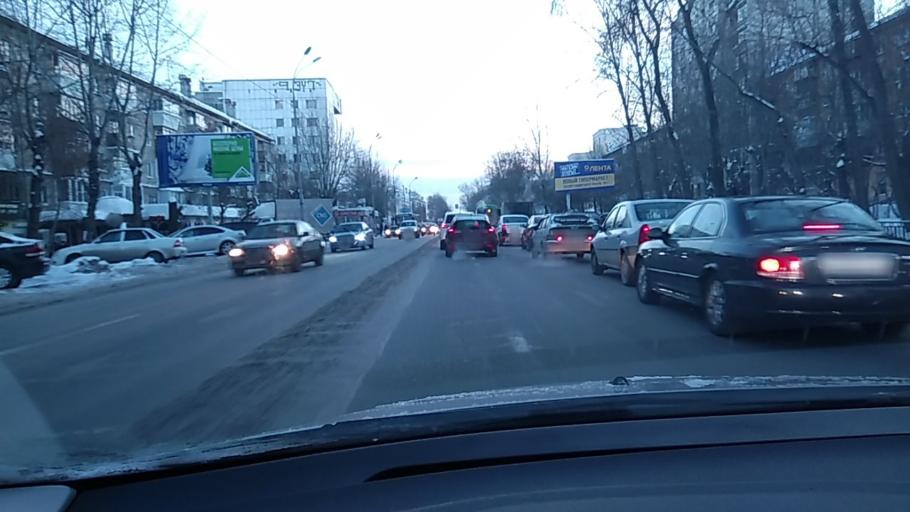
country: RU
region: Sverdlovsk
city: Yekaterinburg
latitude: 56.8279
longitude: 60.6372
